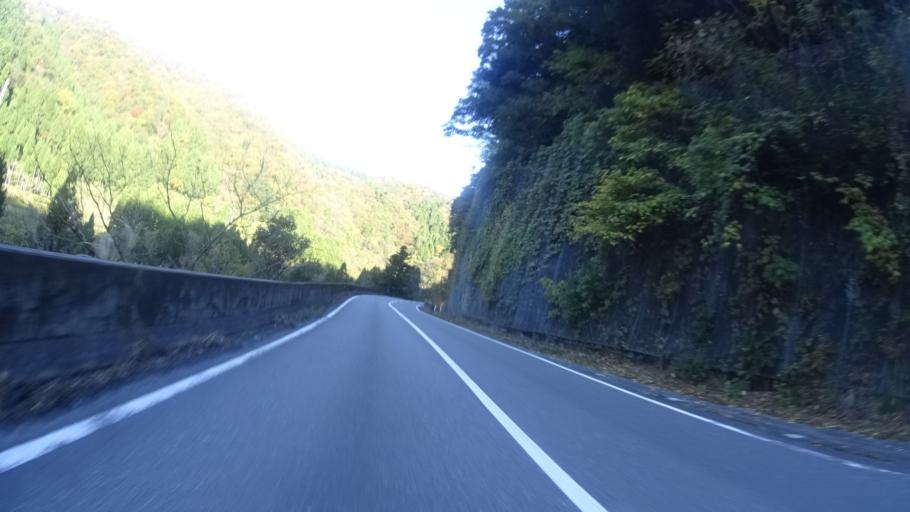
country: JP
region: Fukui
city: Maruoka
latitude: 36.2165
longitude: 136.3526
